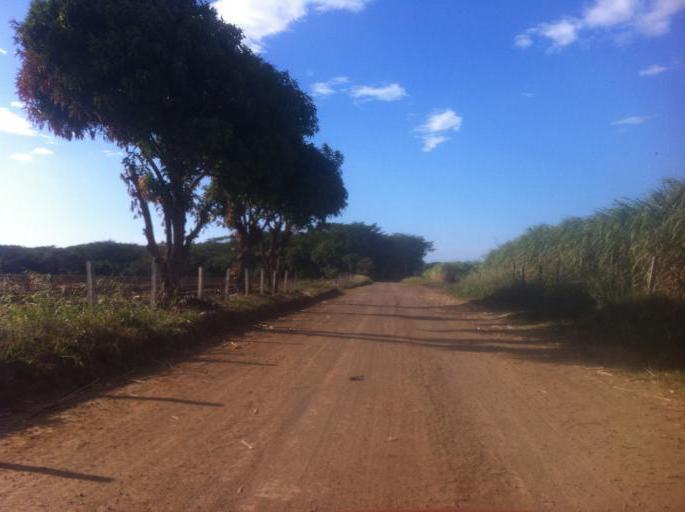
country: NI
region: Managua
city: Masachapa
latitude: 11.8400
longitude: -86.5222
